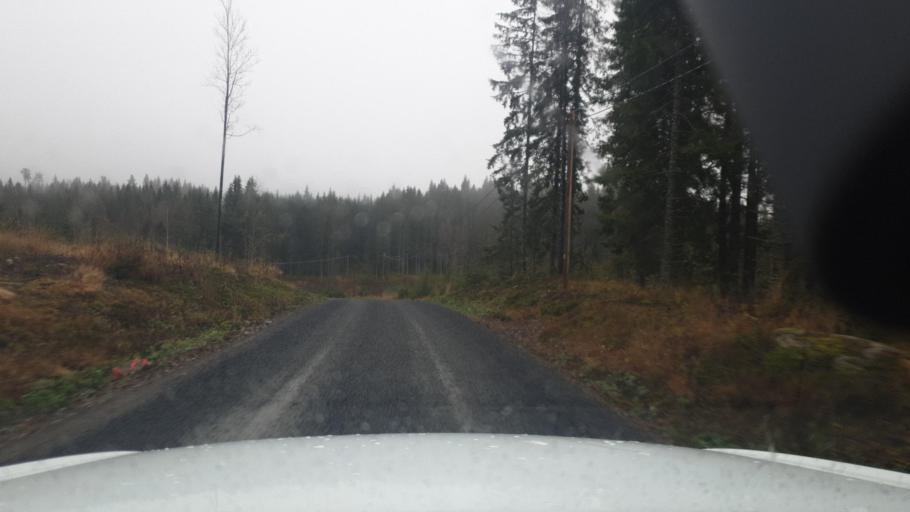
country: SE
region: Vaermland
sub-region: Eda Kommun
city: Charlottenberg
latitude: 60.1480
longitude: 12.5954
